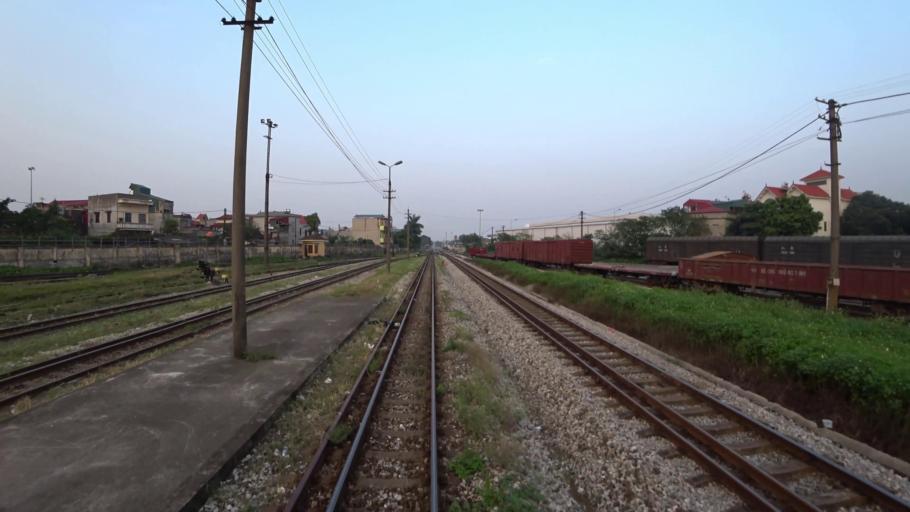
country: VN
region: Ha Noi
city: Dong Anh
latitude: 21.1043
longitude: 105.9026
